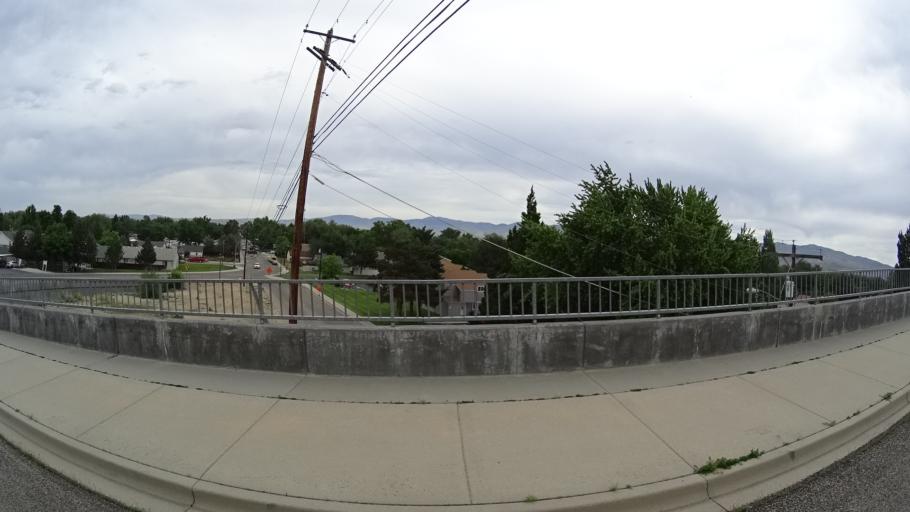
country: US
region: Idaho
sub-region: Ada County
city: Boise
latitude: 43.5787
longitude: -116.2237
